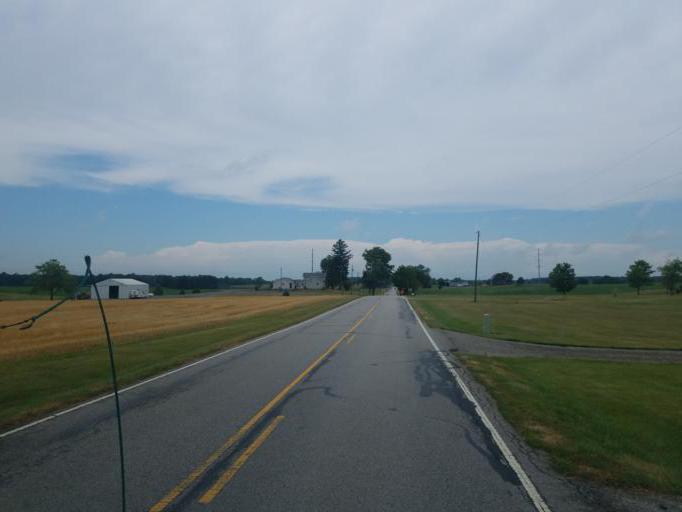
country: US
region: Indiana
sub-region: DeKalb County
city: Butler
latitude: 41.3861
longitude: -84.8559
